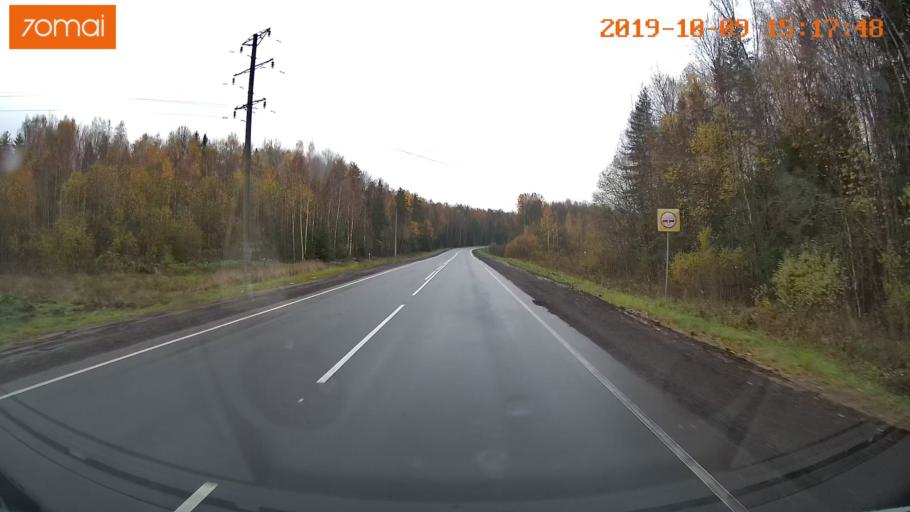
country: RU
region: Kostroma
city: Susanino
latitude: 58.0934
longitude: 41.5814
